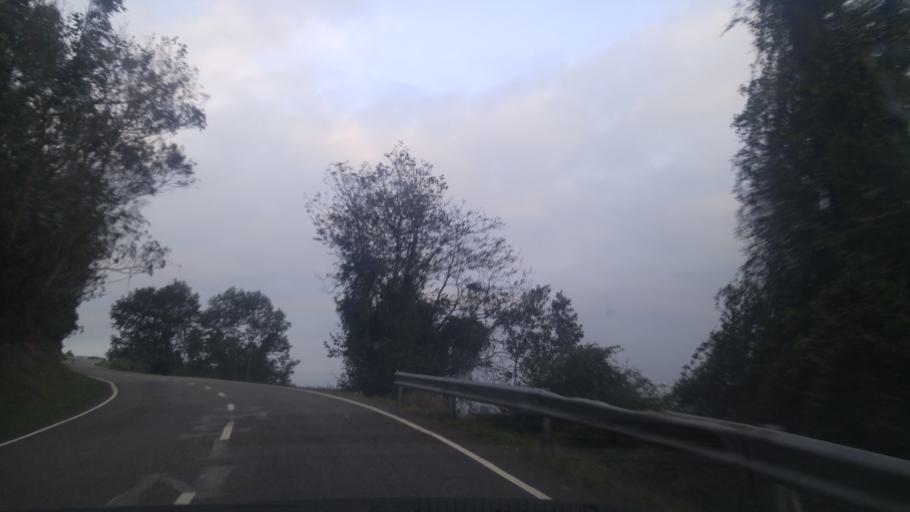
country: ES
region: Asturias
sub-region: Province of Asturias
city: Oviedo
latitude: 43.3824
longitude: -5.8547
